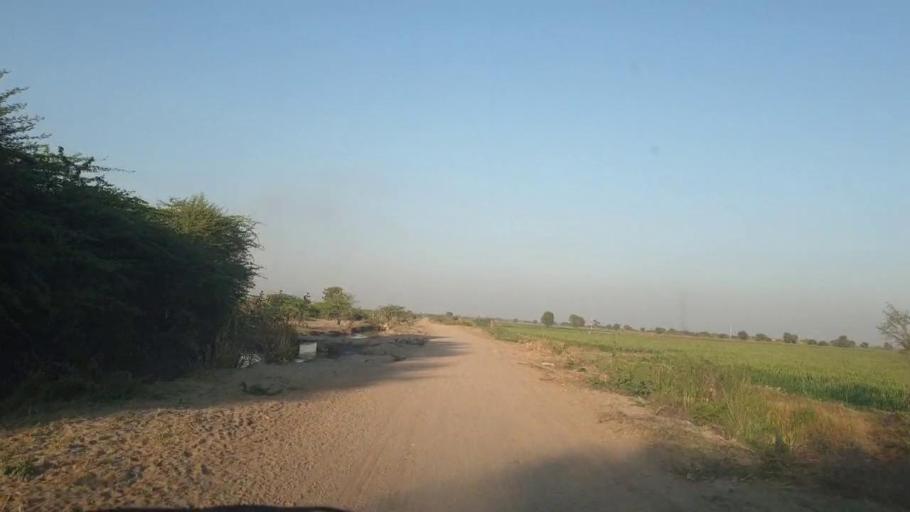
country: PK
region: Sindh
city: Mirpur Khas
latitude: 25.4787
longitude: 69.0875
